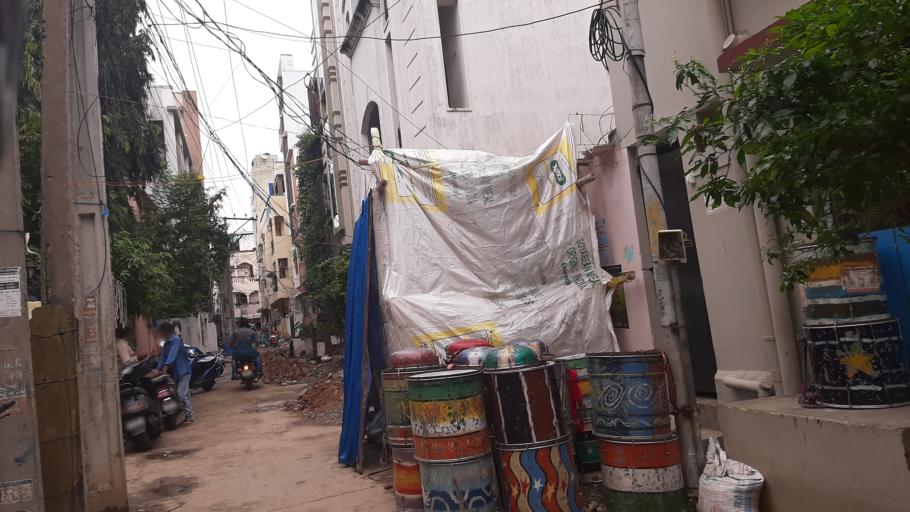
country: IN
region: Andhra Pradesh
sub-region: Vishakhapatnam
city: Yarada
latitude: 17.7242
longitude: 83.3338
